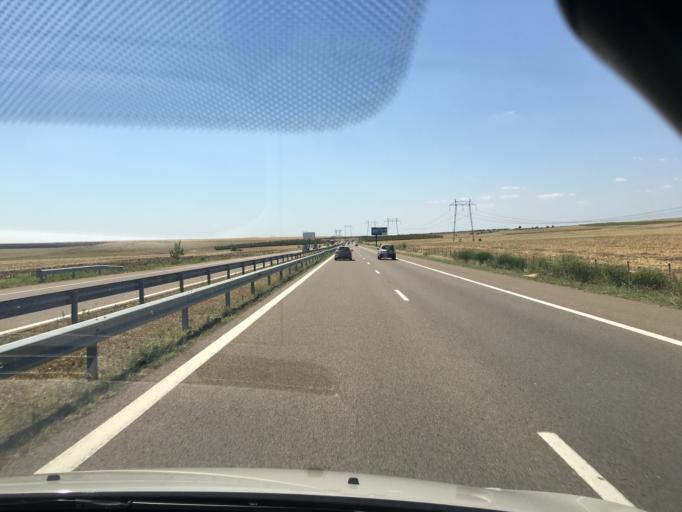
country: BG
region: Burgas
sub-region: Obshtina Kameno
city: Kameno
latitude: 42.5923
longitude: 27.2360
